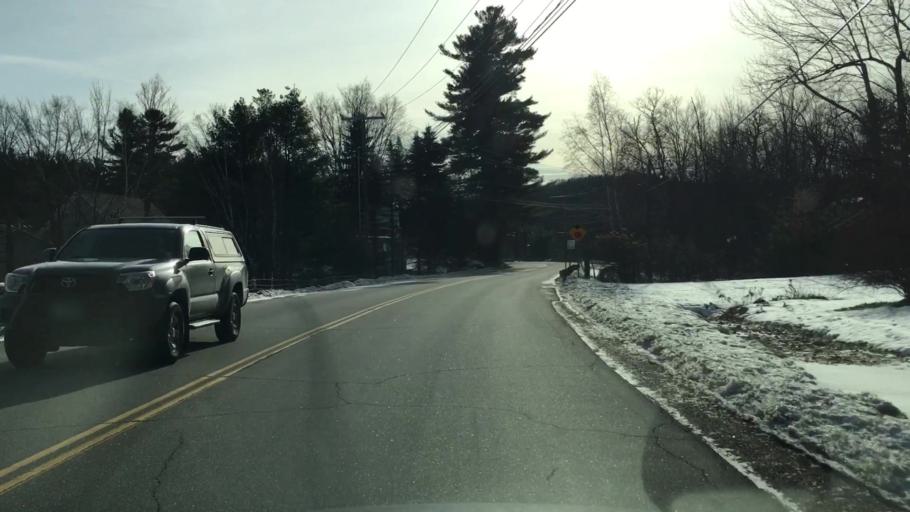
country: US
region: New Hampshire
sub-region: Sullivan County
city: Sunapee
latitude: 43.4333
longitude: -72.0662
